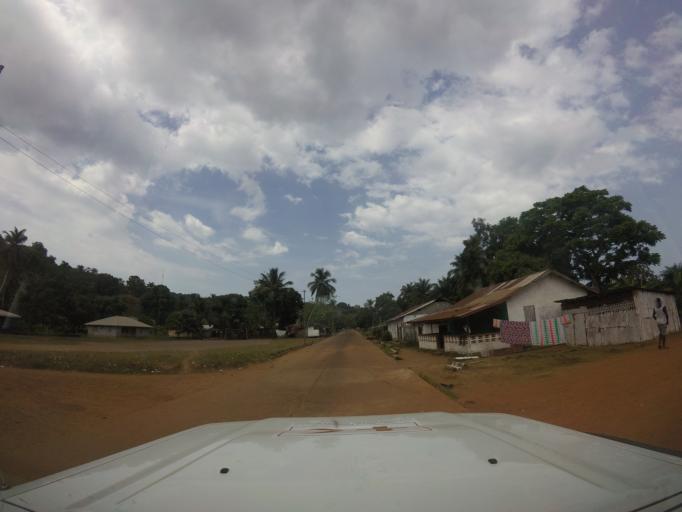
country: LR
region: Grand Cape Mount
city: Robertsport
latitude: 6.7548
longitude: -11.3709
